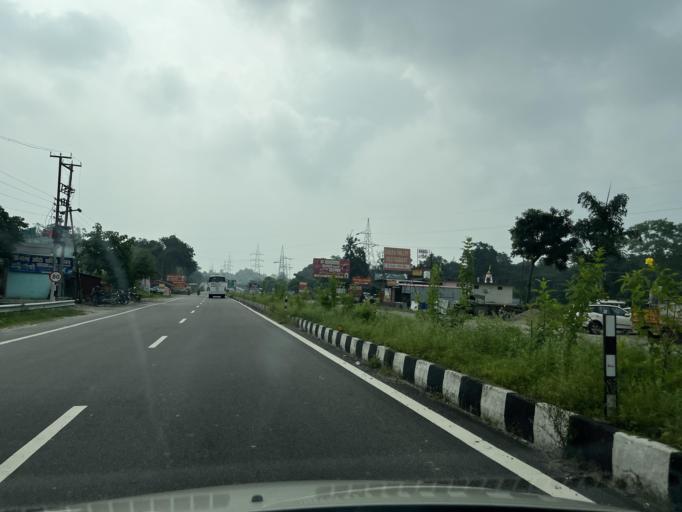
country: IN
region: Uttarakhand
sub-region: Dehradun
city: Raiwala
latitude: 30.0729
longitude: 78.2019
